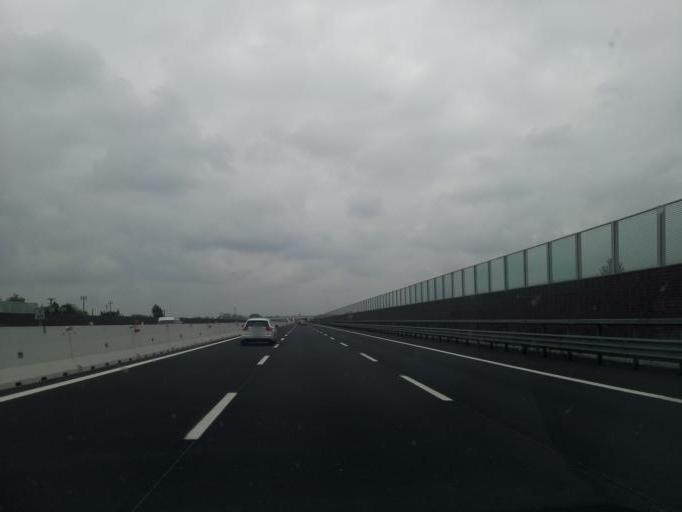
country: IT
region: Veneto
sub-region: Provincia di Venezia
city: Fossalta di Piave
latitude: 45.6554
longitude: 12.4949
